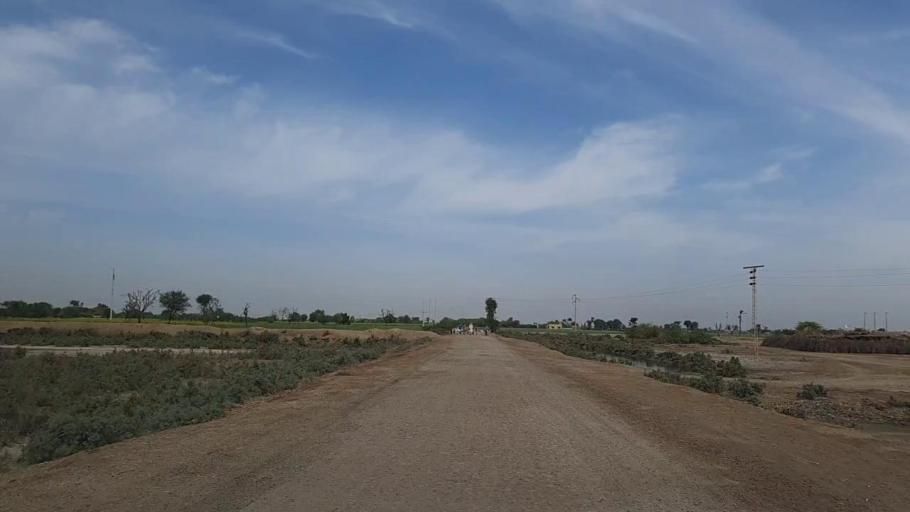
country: PK
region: Sindh
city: Samaro
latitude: 25.2953
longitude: 69.4238
